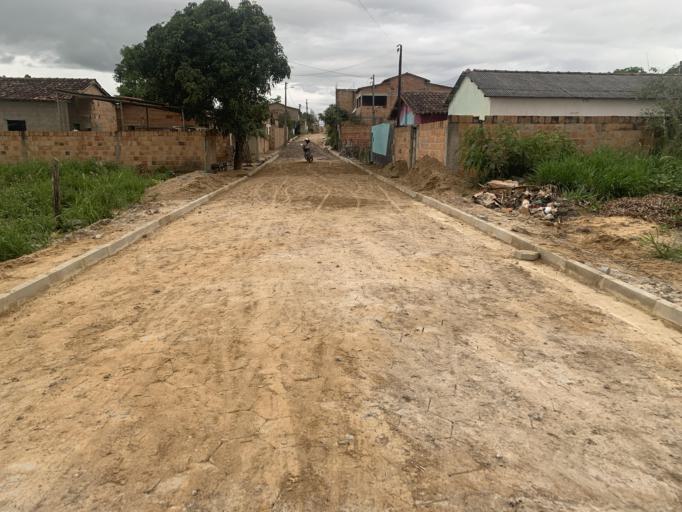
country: BR
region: Bahia
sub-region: Medeiros Neto
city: Medeiros Neto
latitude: -17.3918
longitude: -40.2322
